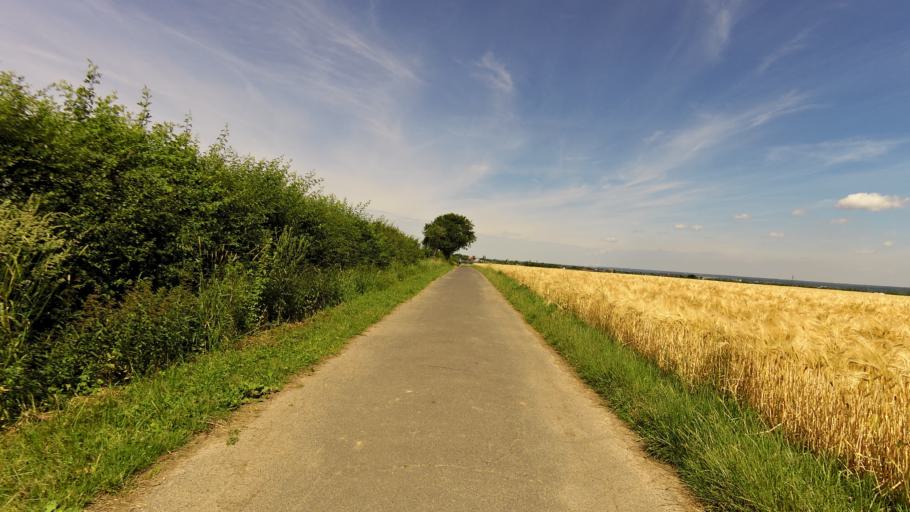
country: DE
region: North Rhine-Westphalia
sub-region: Regierungsbezirk Koln
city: Rheinbach
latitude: 50.6105
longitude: 6.9664
